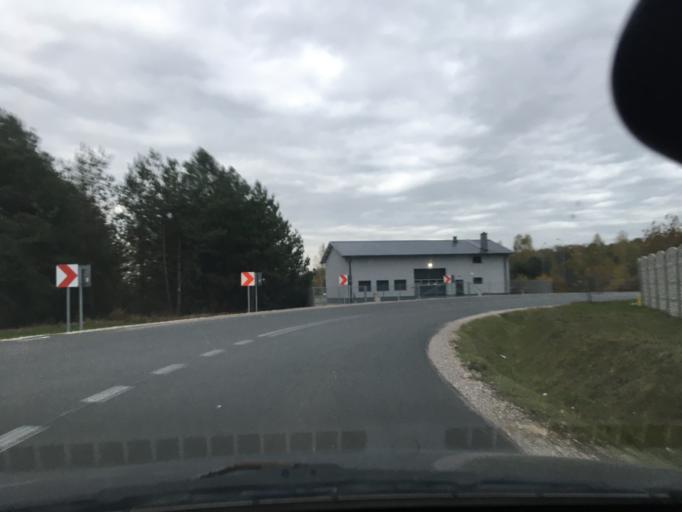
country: PL
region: Lodz Voivodeship
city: Zabia Wola
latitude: 52.0492
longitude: 20.7197
